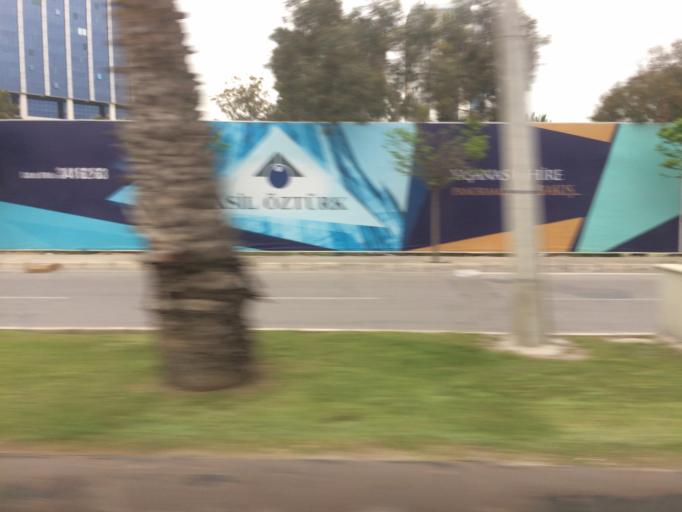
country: TR
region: Izmir
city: Izmir
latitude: 38.4520
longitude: 27.1694
